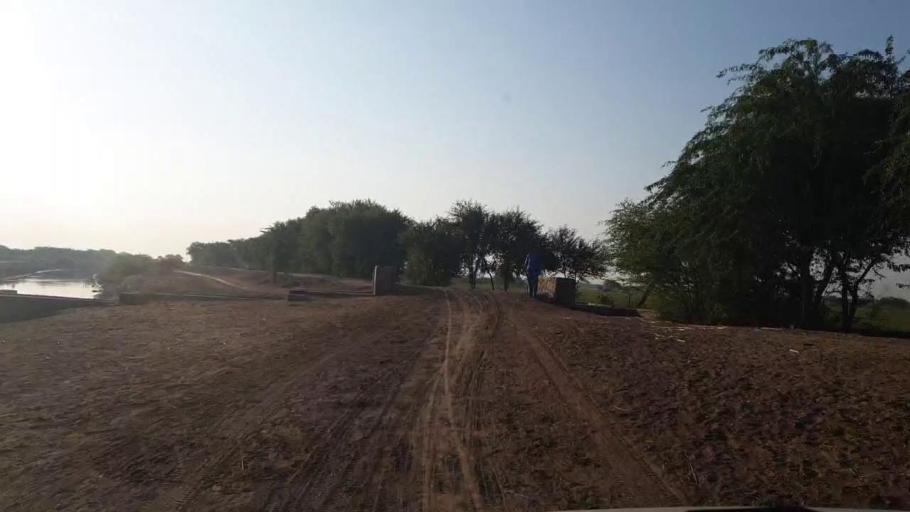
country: PK
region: Sindh
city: Badin
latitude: 24.6375
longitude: 68.7921
